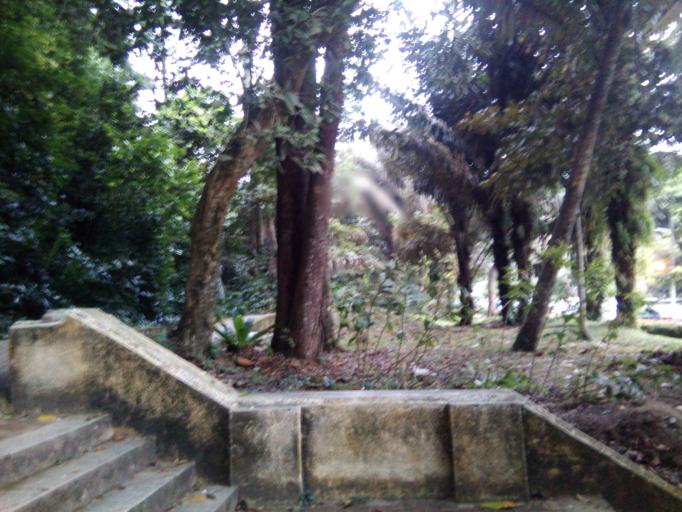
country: MY
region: Penang
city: Tanjung Tokong
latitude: 5.4361
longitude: 100.2929
